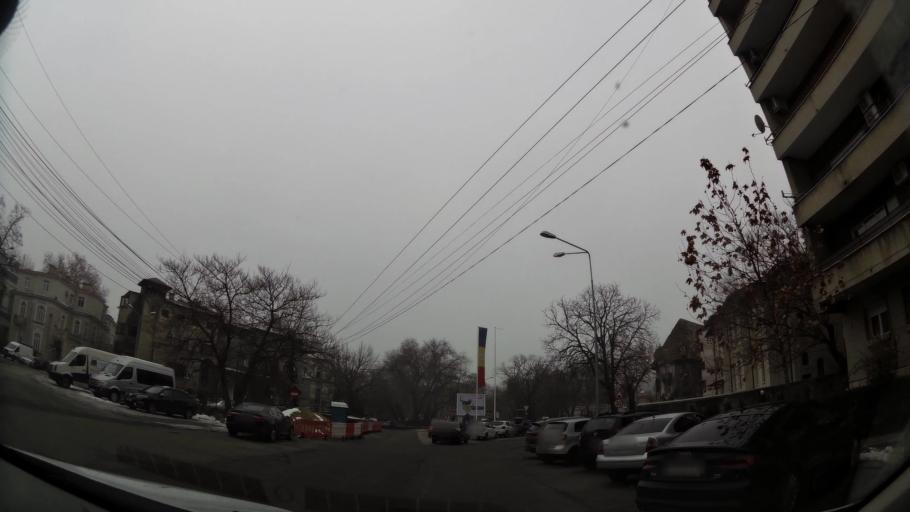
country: RO
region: Bucuresti
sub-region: Municipiul Bucuresti
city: Bucharest
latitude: 44.4449
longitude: 26.1037
